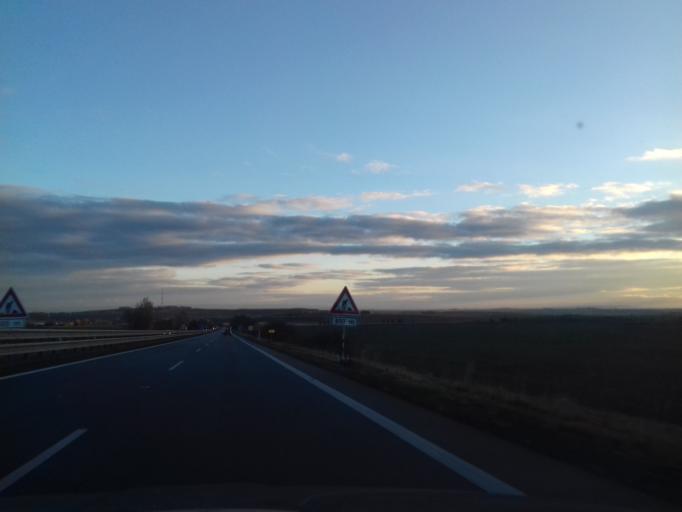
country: CZ
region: Olomoucky
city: Otaslavice
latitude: 49.3538
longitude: 17.0770
